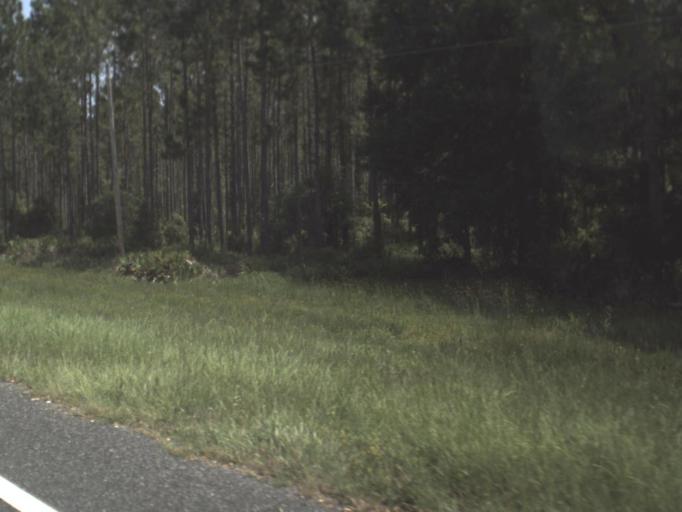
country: US
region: Florida
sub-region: Taylor County
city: Steinhatchee
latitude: 29.7445
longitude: -83.3198
